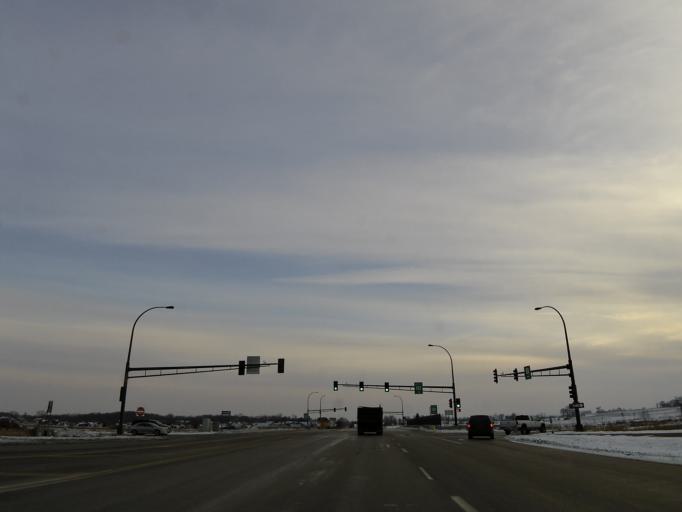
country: US
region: Minnesota
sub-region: Carver County
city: Carver
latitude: 44.7784
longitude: -93.6426
